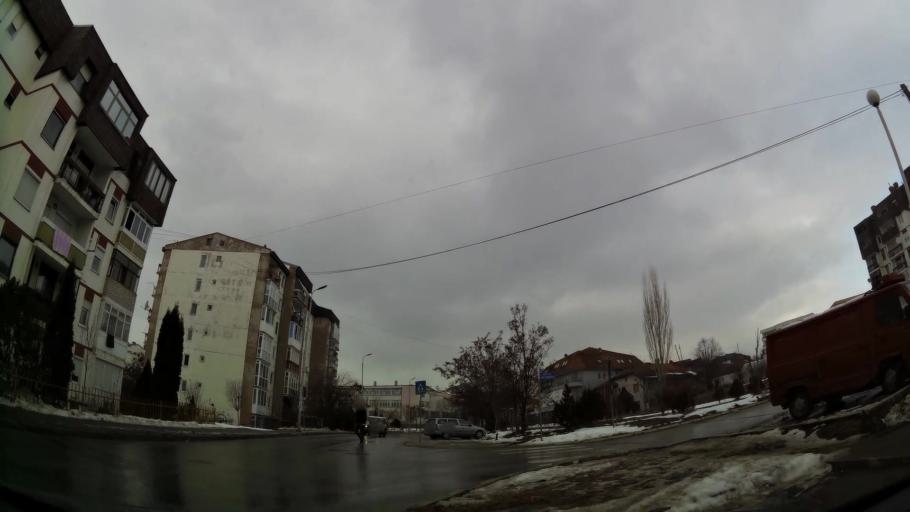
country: XK
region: Pristina
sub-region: Komuna e Prishtines
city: Pristina
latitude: 42.6575
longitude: 21.1813
